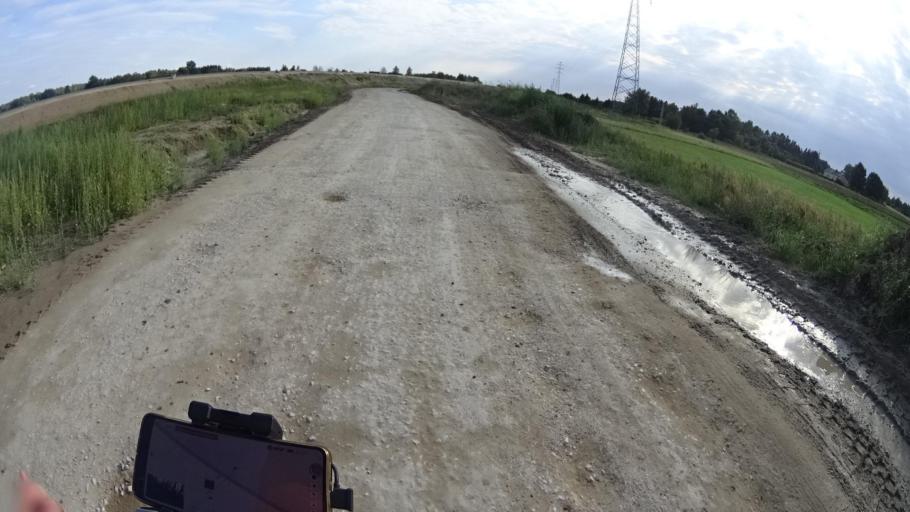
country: PL
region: Masovian Voivodeship
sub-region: Powiat piaseczynski
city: Tarczyn
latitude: 51.9896
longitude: 20.8776
